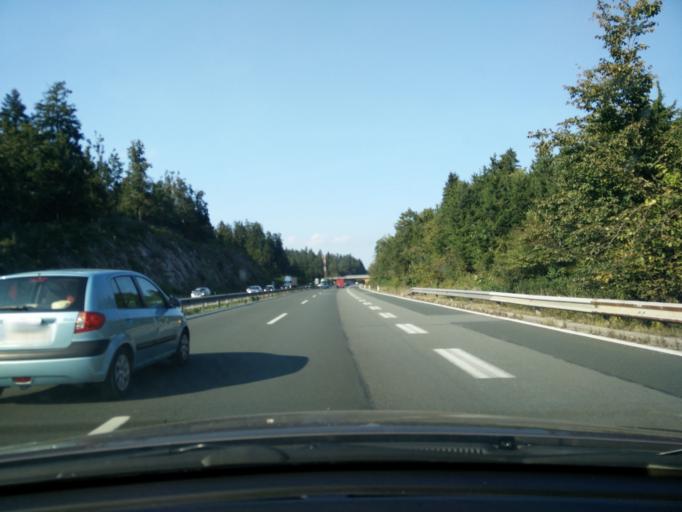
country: SI
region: Logatec
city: Logatec
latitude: 45.9039
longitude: 14.2564
